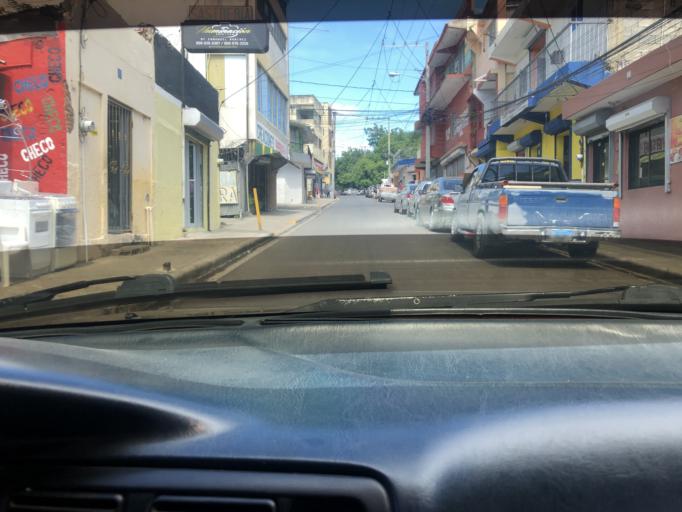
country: DO
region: Santiago
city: Santiago de los Caballeros
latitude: 19.4501
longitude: -70.7099
